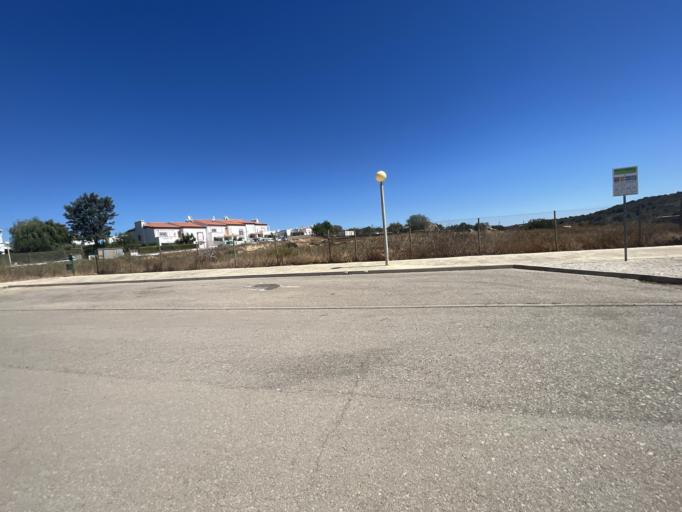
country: PT
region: Faro
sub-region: Portimao
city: Portimao
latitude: 37.1266
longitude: -8.5121
